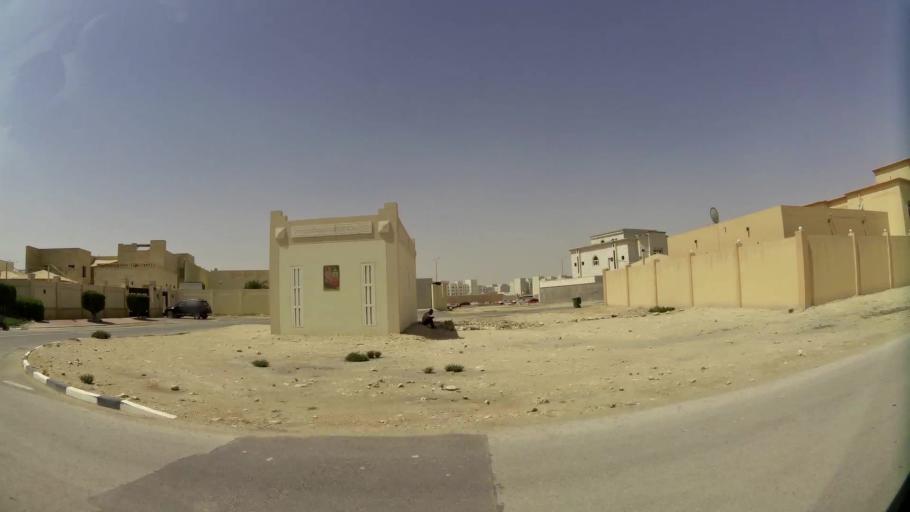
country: QA
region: Baladiyat Umm Salal
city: Umm Salal Muhammad
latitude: 25.3662
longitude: 51.4757
